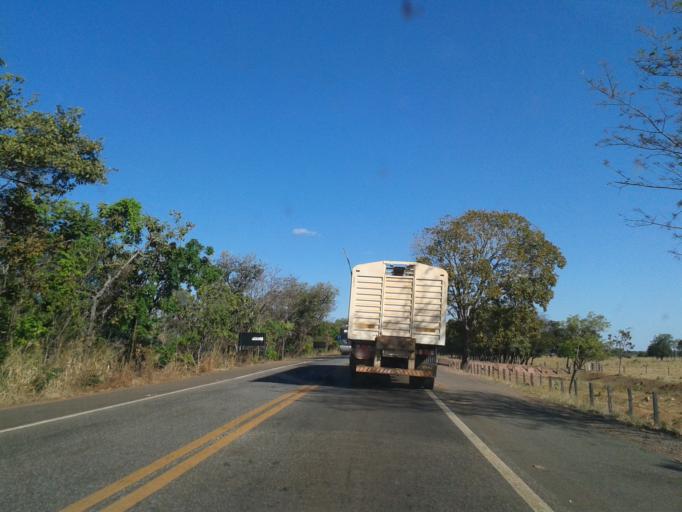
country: BR
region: Goias
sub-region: Mozarlandia
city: Mozarlandia
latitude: -14.8075
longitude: -50.5330
